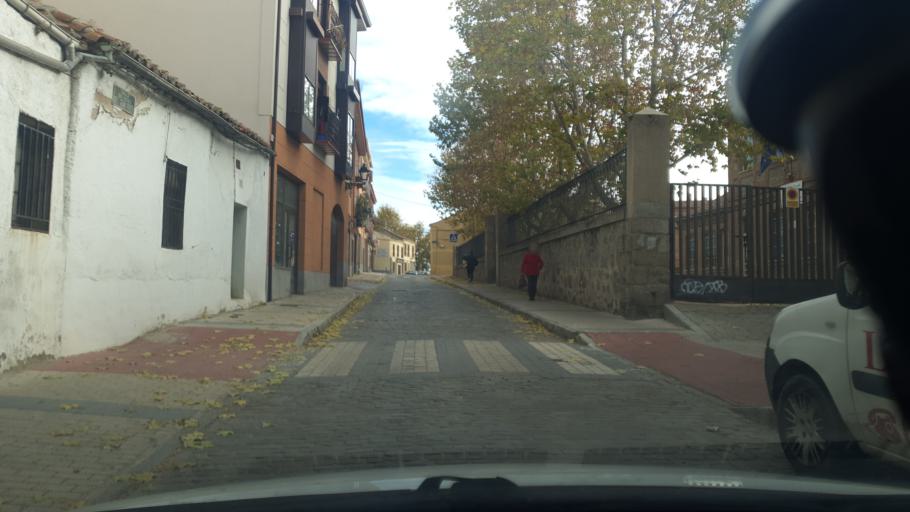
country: ES
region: Castille and Leon
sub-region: Provincia de Avila
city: Avila
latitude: 40.6525
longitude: -4.6958
